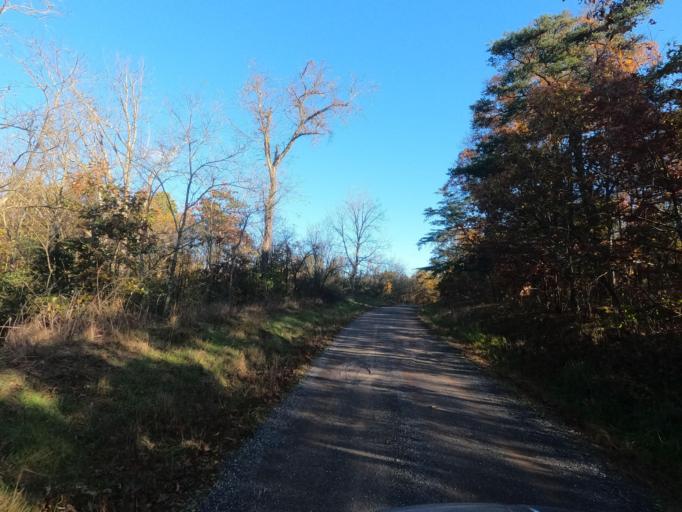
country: US
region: West Virginia
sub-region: Mineral County
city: Fort Ashby
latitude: 39.5421
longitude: -78.5321
